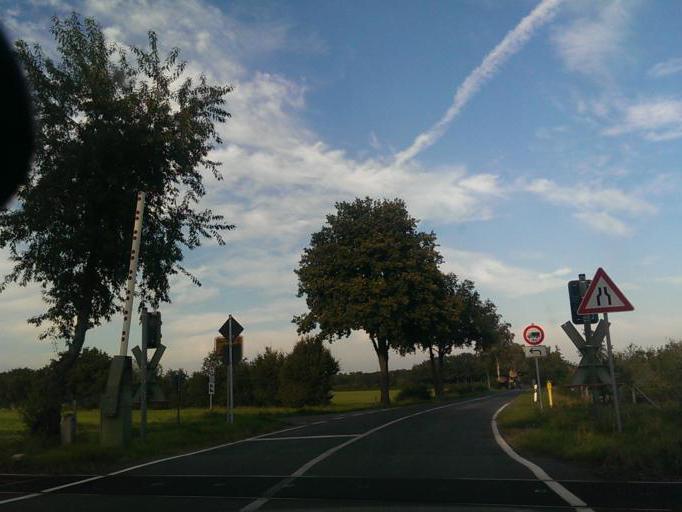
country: DE
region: Lower Saxony
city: Lindwedel
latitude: 52.5969
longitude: 9.7120
